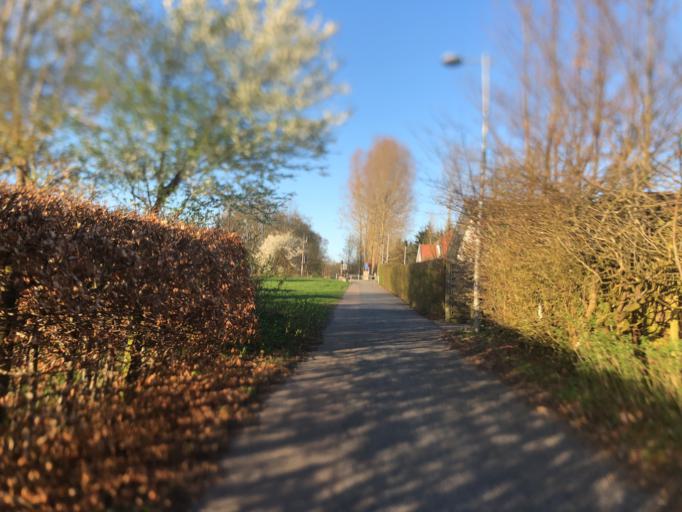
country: DK
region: Zealand
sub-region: Ringsted Kommune
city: Ringsted
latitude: 55.4644
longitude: 11.7994
